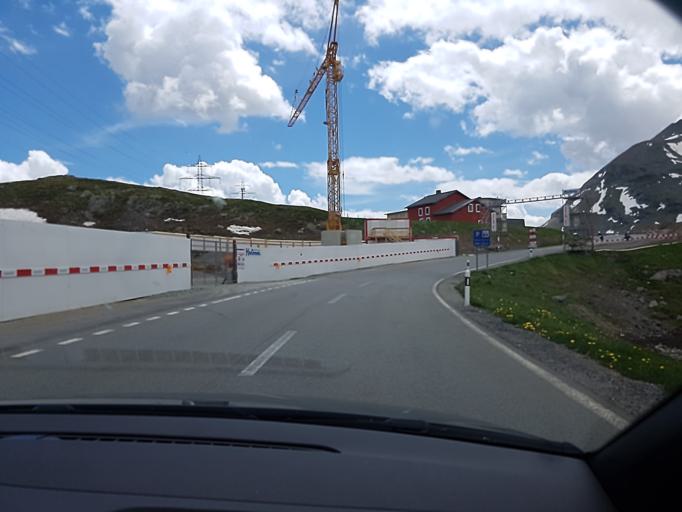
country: CH
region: Grisons
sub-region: Bernina District
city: Poschiavo
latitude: 46.4129
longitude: 10.0212
